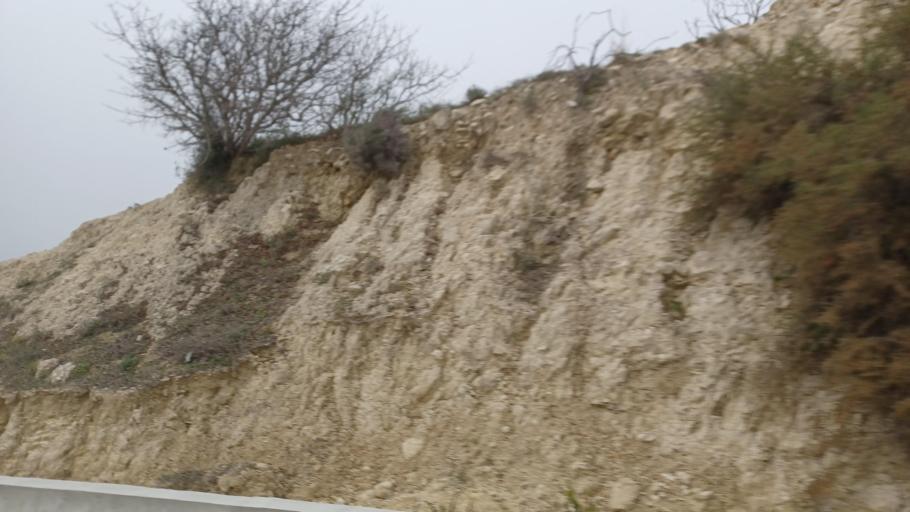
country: CY
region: Limassol
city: Pissouri
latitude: 34.7117
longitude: 32.7445
